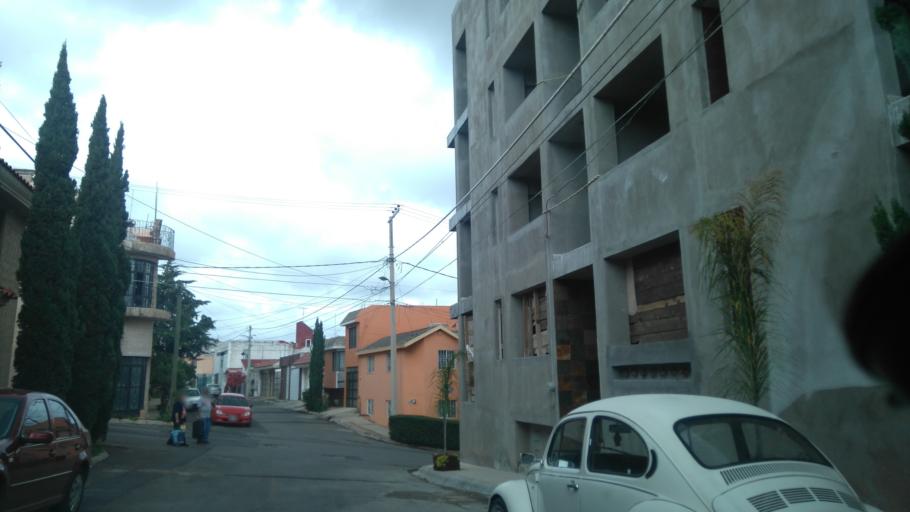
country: MX
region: Zacatecas
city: Zacatecas
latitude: 22.7563
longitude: -102.5888
